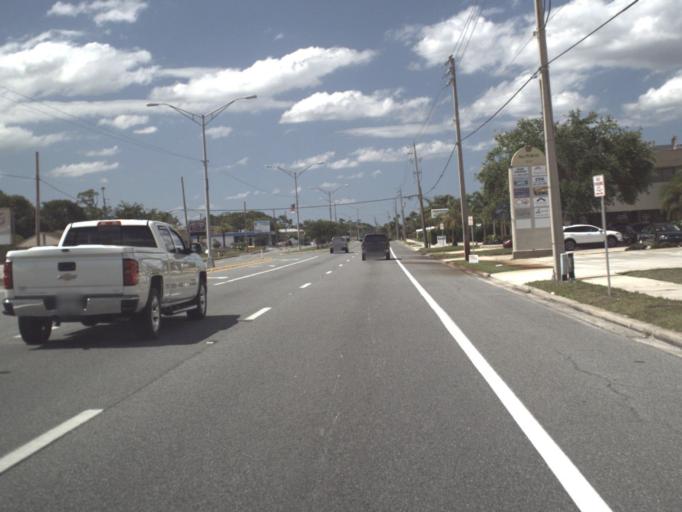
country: US
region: Florida
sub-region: Brevard County
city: Titusville
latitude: 28.5875
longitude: -80.8020
